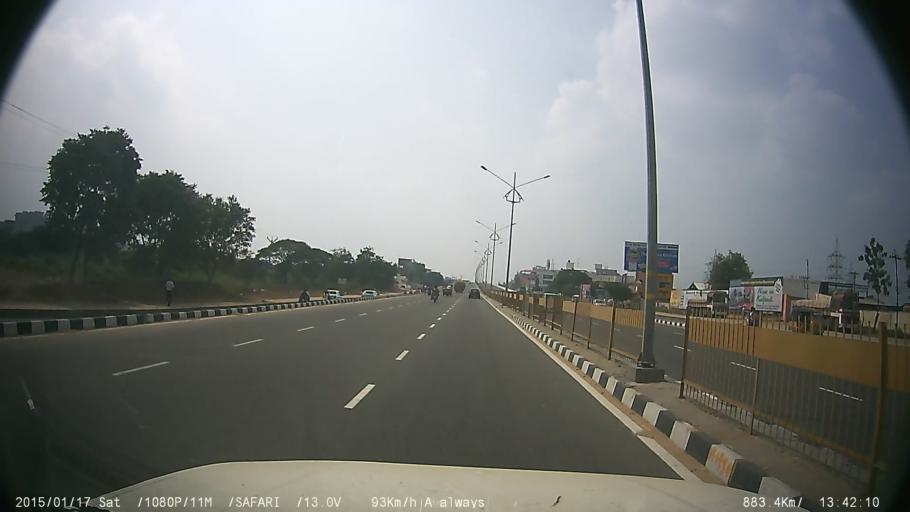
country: IN
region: Tamil Nadu
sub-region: Vellore
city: Vellore
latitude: 12.9338
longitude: 79.1436
